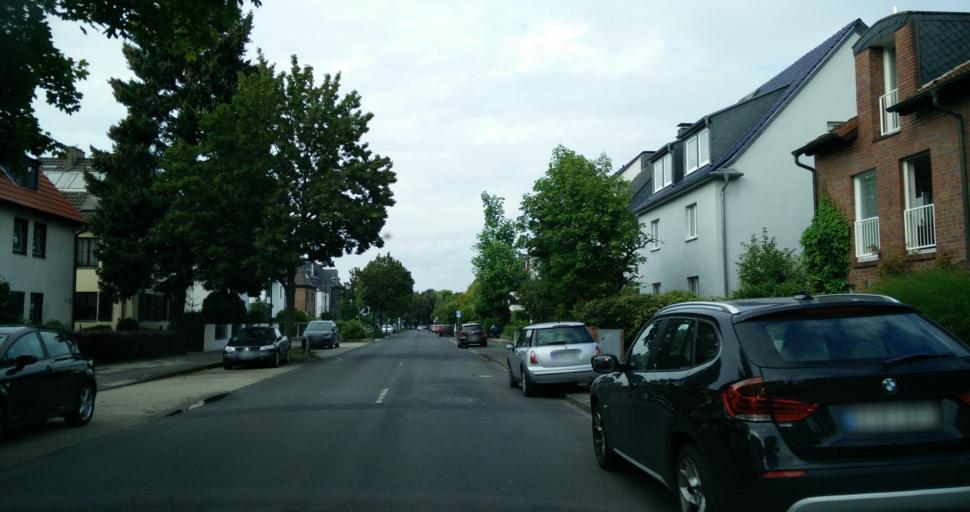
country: DE
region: North Rhine-Westphalia
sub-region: Regierungsbezirk Dusseldorf
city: Meerbusch
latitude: 51.2944
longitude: 6.7407
